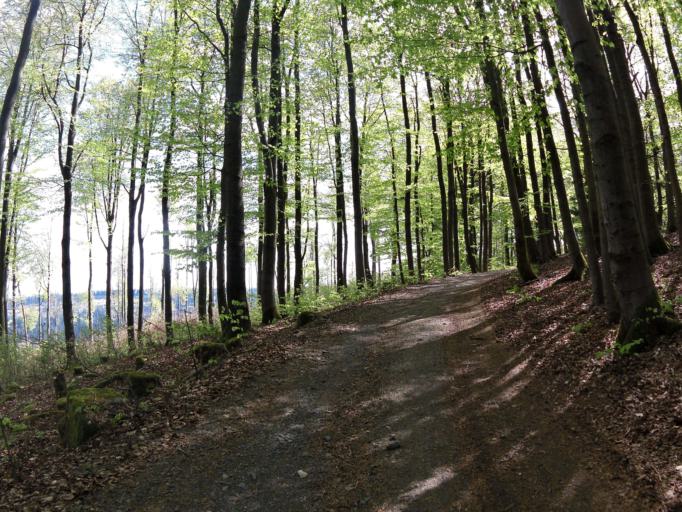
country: DE
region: Thuringia
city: Finsterbergen
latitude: 50.7976
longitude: 10.5406
